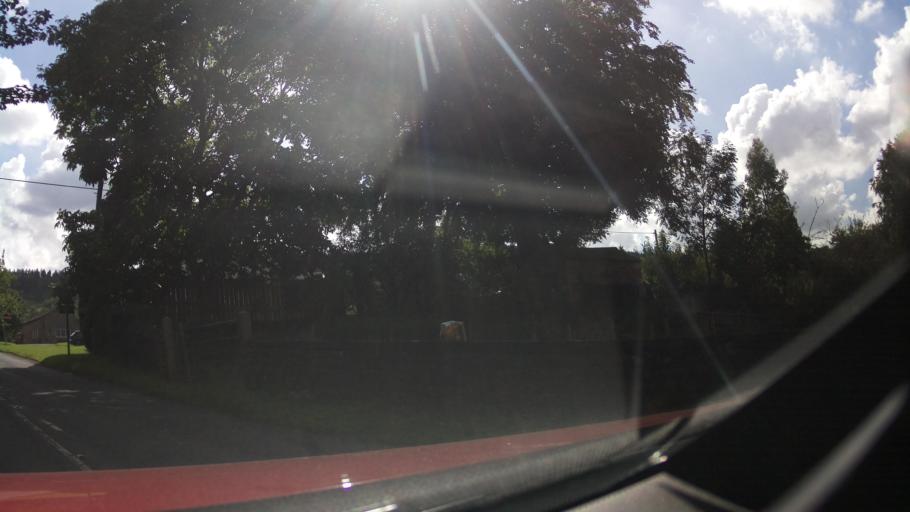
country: GB
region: England
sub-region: North Yorkshire
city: Leyburn
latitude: 54.2704
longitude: -1.7795
